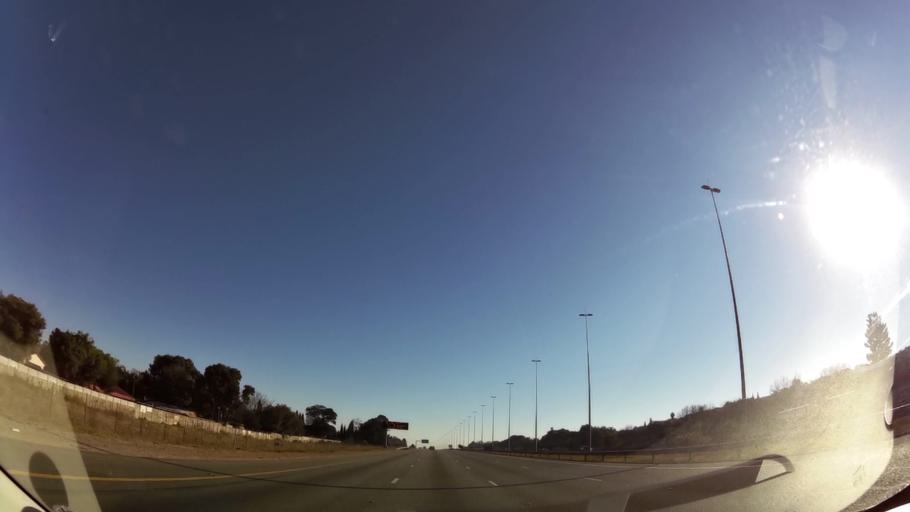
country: ZA
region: Gauteng
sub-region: City of Tshwane Metropolitan Municipality
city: Centurion
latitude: -25.8477
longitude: 28.2505
